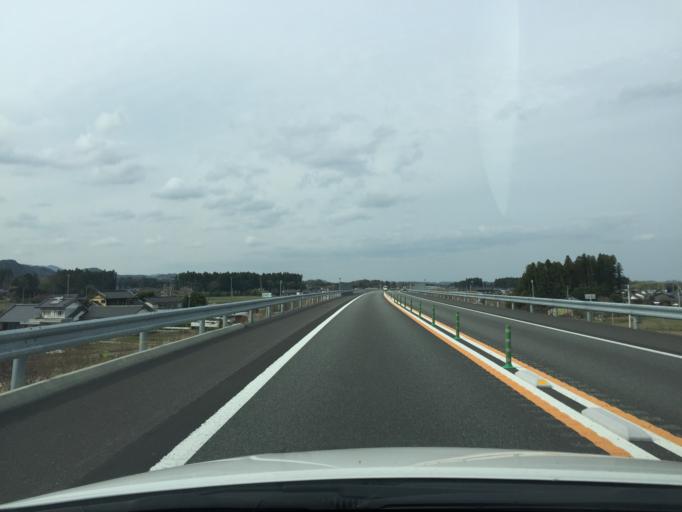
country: JP
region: Fukushima
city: Namie
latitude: 37.6045
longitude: 140.9253
